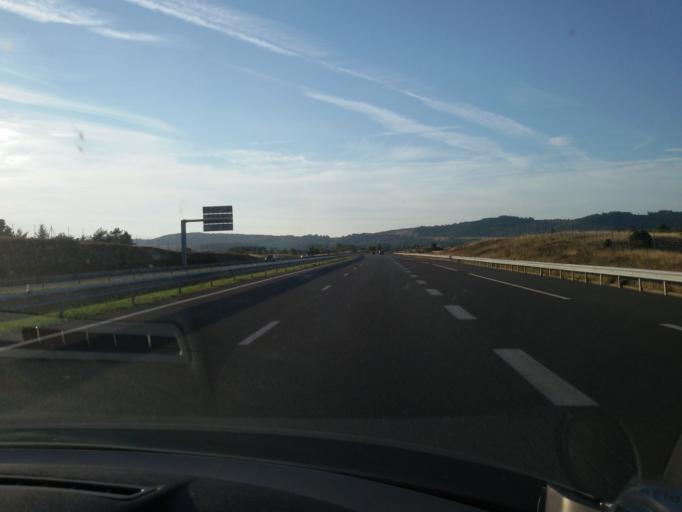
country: FR
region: Midi-Pyrenees
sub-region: Departement de l'Aveyron
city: La Cavalerie
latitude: 43.9526
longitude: 3.2150
